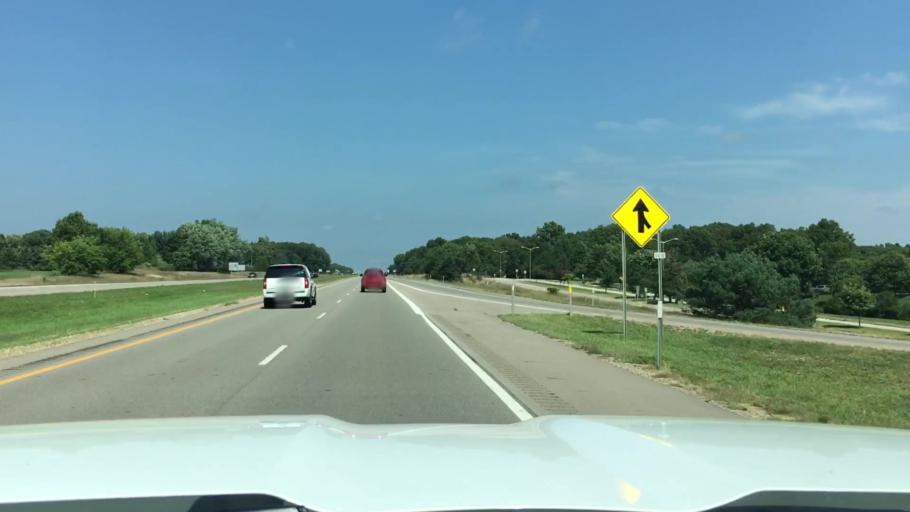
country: US
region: Michigan
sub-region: Kalamazoo County
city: Portage
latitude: 42.2018
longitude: -85.6450
